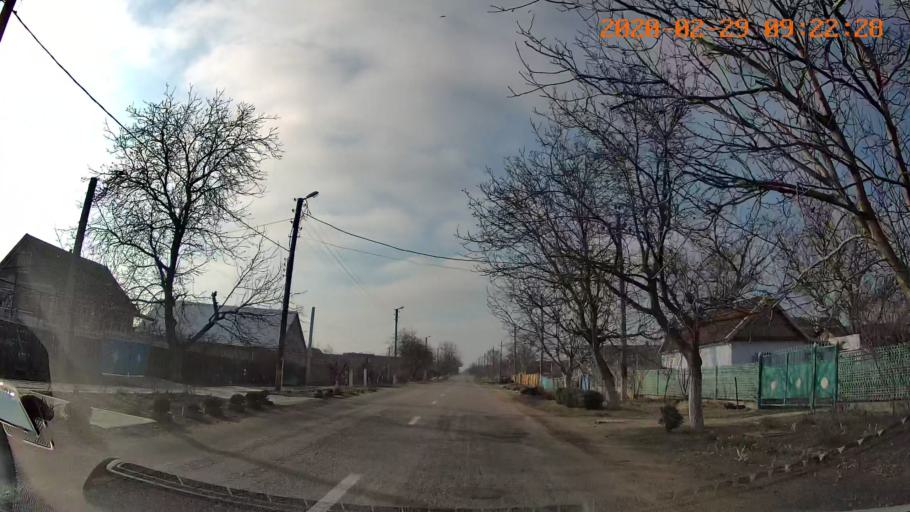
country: MD
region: Telenesti
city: Pervomaisc
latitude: 46.7350
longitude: 29.9640
